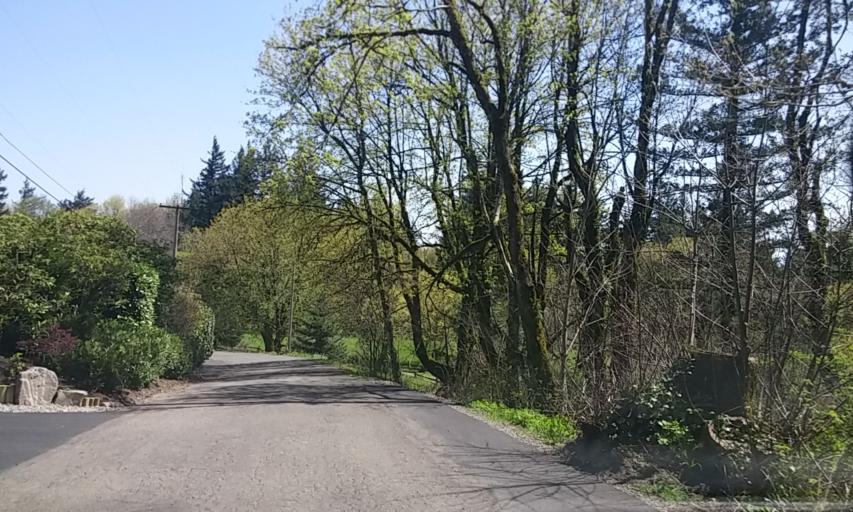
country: US
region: Oregon
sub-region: Washington County
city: West Haven-Sylvan
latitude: 45.5260
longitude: -122.7508
